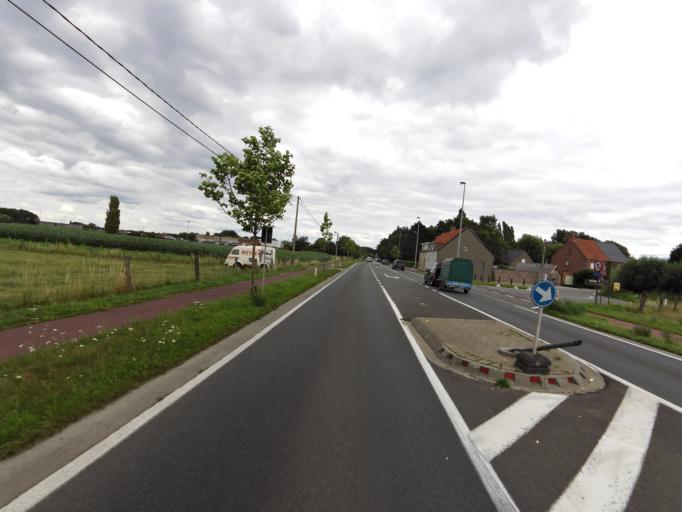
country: BE
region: Flanders
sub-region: Provincie West-Vlaanderen
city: Hooglede
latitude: 50.9589
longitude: 3.0747
